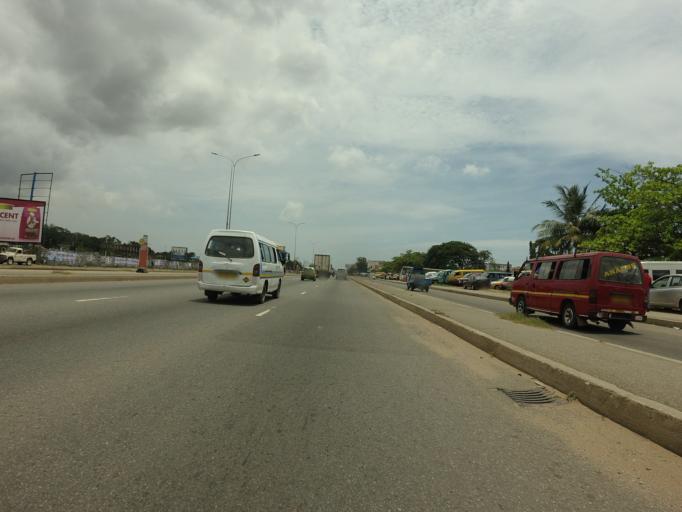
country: GH
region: Greater Accra
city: Accra
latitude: 5.5718
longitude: -0.2470
